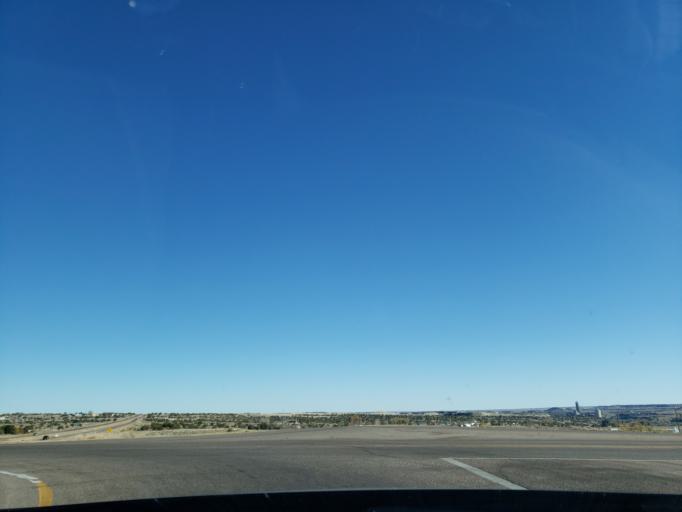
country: US
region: Colorado
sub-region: Fremont County
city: Penrose
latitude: 38.4181
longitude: -105.0427
